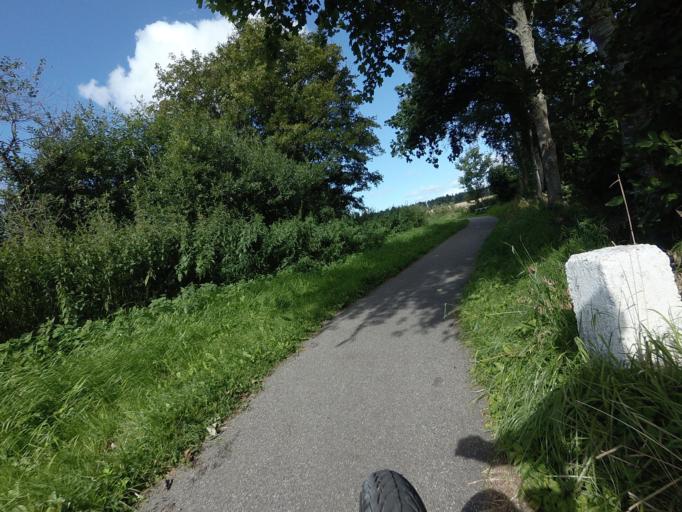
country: DK
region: Central Jutland
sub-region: Horsens Kommune
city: Braedstrup
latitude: 55.9841
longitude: 9.6632
